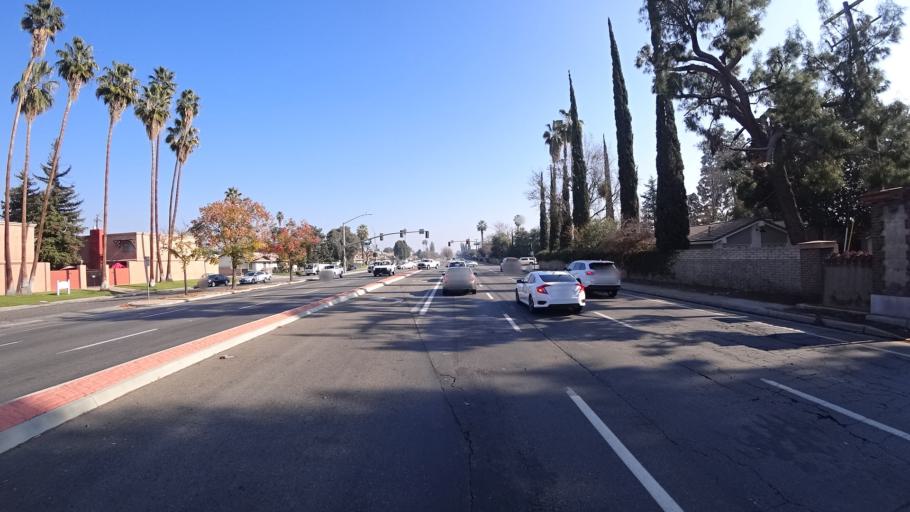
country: US
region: California
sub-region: Kern County
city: Greenacres
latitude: 35.3543
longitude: -119.0745
